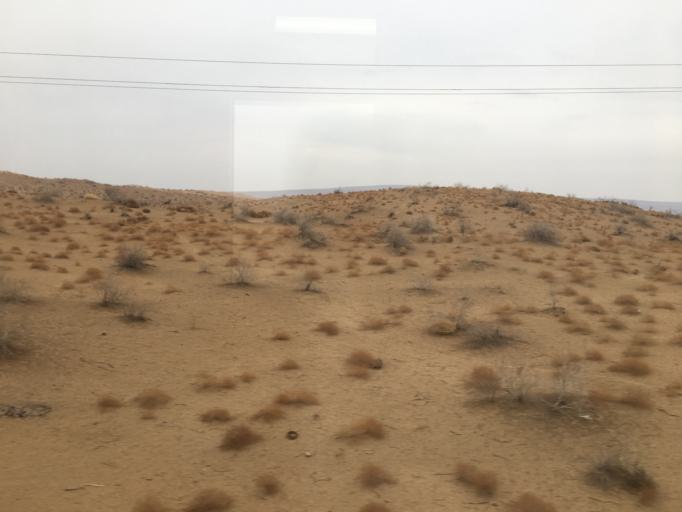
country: TM
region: Mary
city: Yoloeten
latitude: 36.4391
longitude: 62.5869
